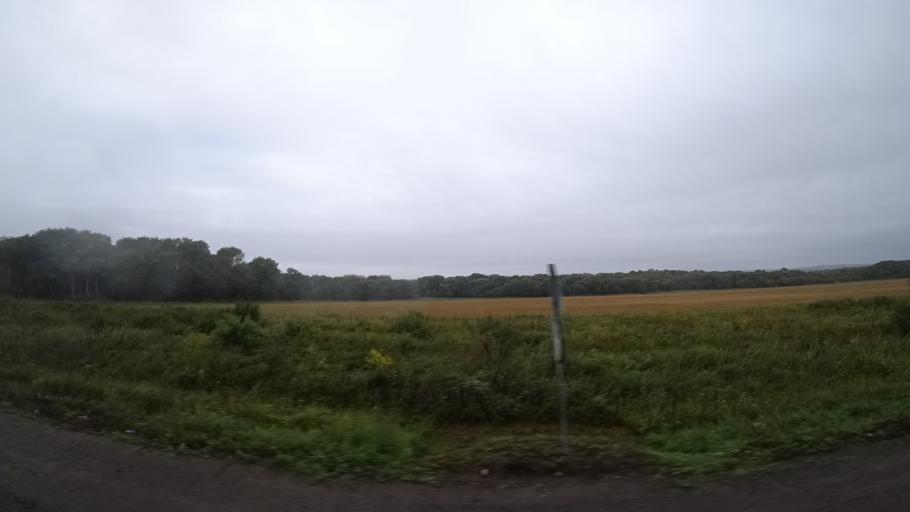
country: RU
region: Primorskiy
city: Monastyrishche
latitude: 44.2784
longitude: 132.4889
